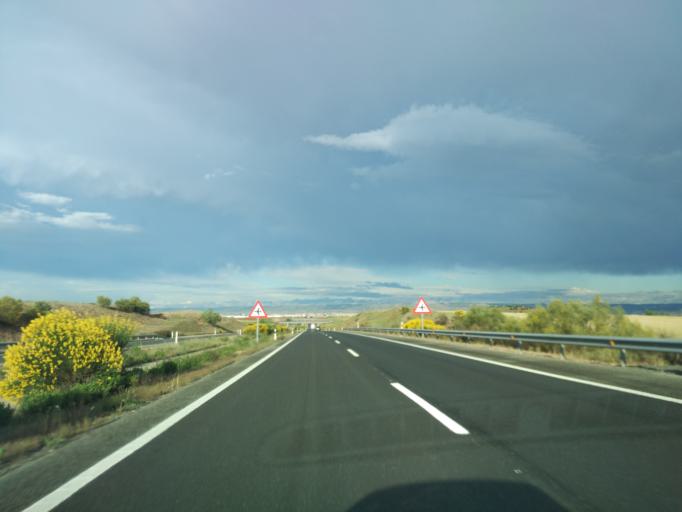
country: ES
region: Madrid
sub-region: Provincia de Madrid
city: Ajalvir
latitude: 40.5060
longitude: -3.4706
